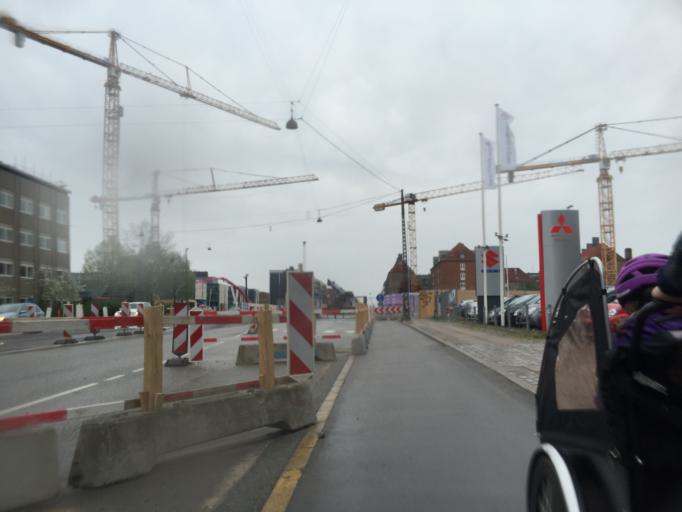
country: DK
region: Capital Region
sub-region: Kobenhavn
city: Copenhagen
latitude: 55.7024
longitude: 12.5578
